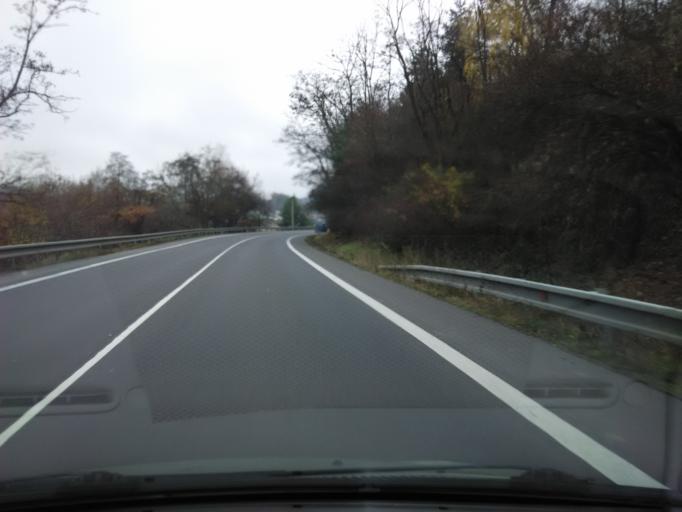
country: SK
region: Banskobystricky
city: Ziar nad Hronom
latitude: 48.5992
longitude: 18.8914
